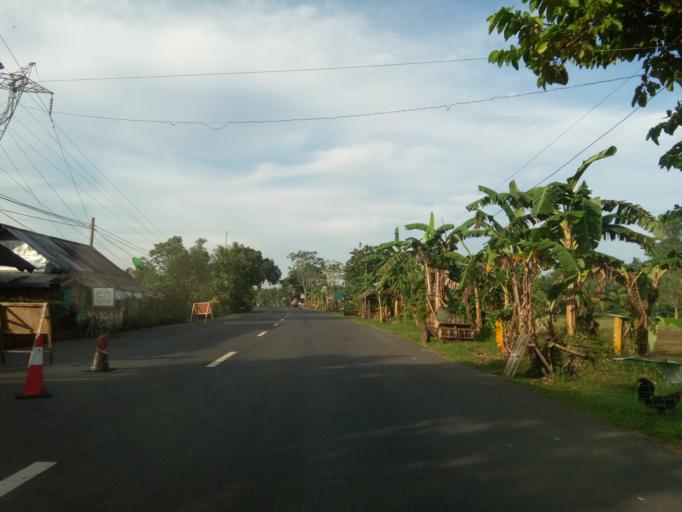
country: PH
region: Caraga
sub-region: Province of Surigao del Norte
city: Tubod
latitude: 9.5480
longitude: 125.5664
